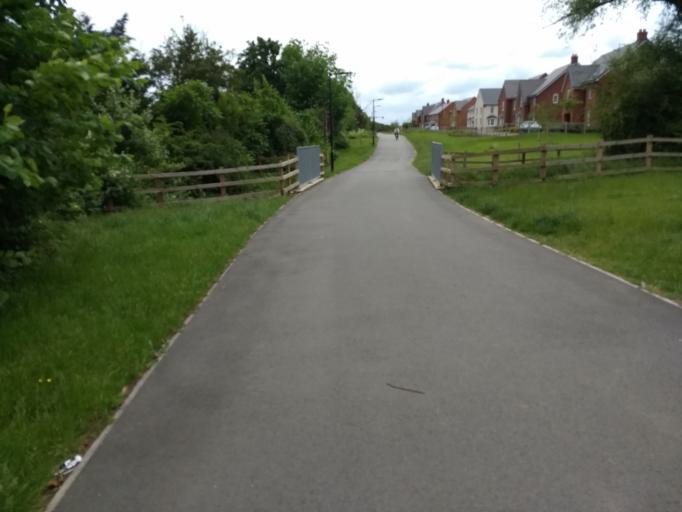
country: GB
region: England
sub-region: Bedford
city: Kempston
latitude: 52.1111
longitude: -0.5149
